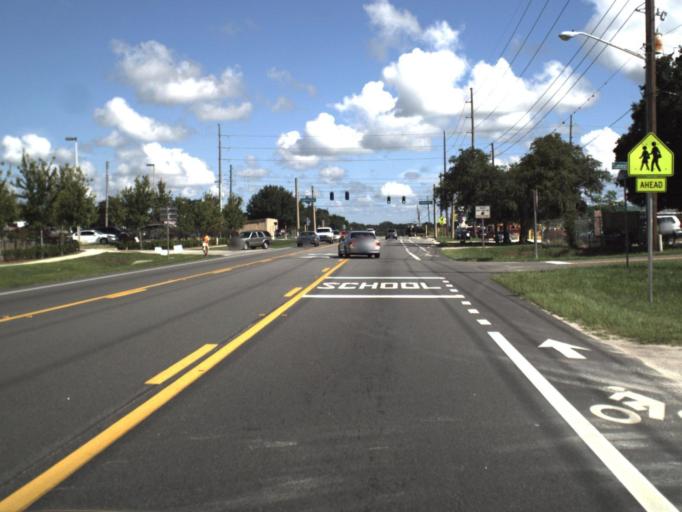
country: US
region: Florida
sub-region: Polk County
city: Haines City
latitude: 28.1125
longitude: -81.6180
